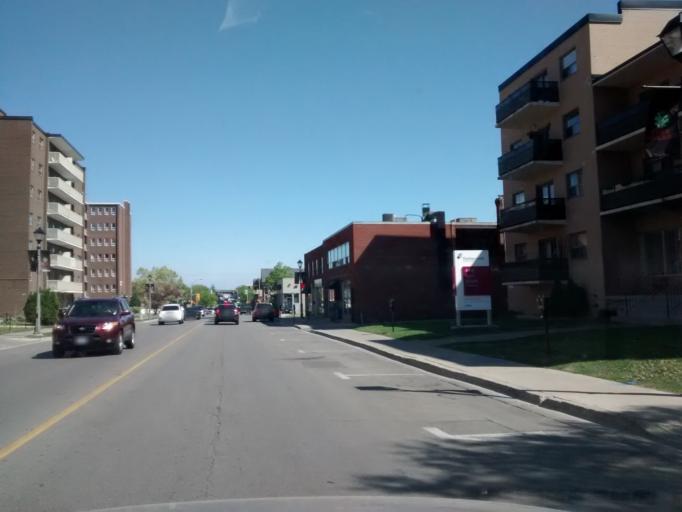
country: CA
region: Ontario
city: Oakville
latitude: 43.4457
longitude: -79.6852
